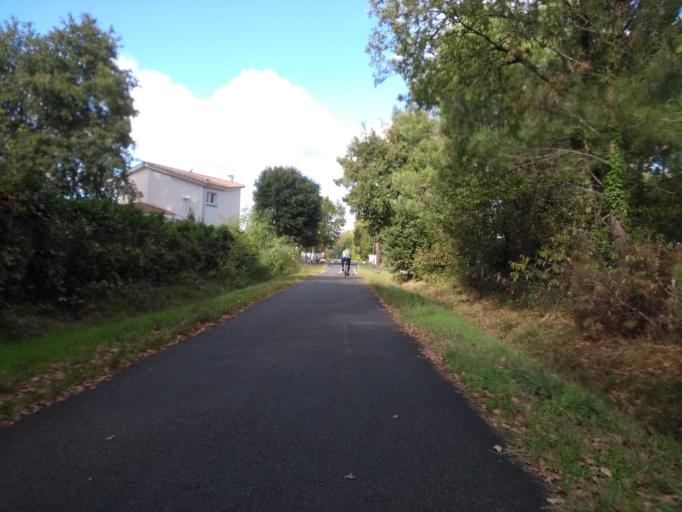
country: FR
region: Aquitaine
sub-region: Departement de la Gironde
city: Saint-Aubin-de-Medoc
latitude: 44.7887
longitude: -0.7005
